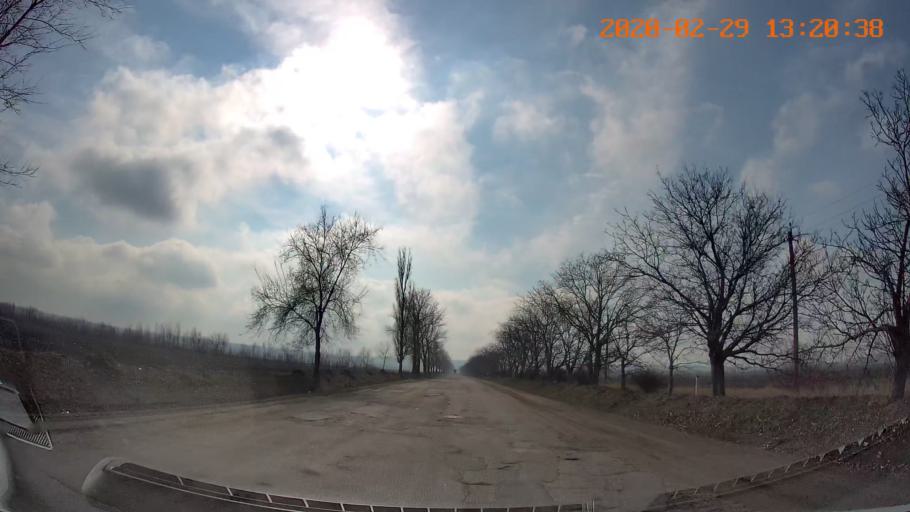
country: MD
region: Telenesti
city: Camenca
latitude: 47.9771
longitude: 28.6397
